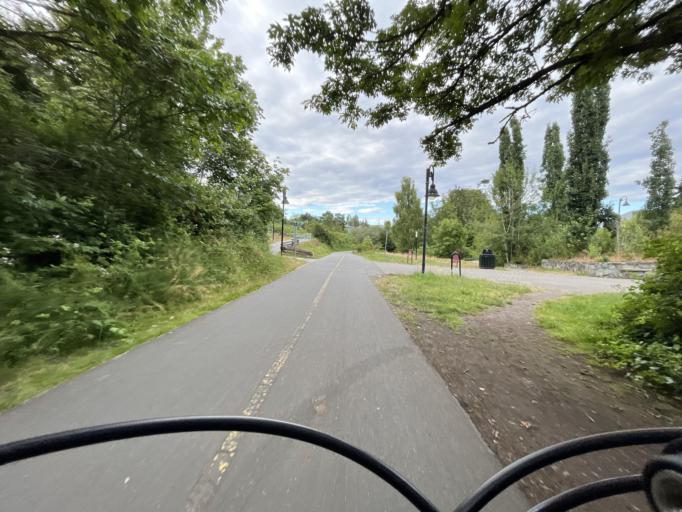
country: CA
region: British Columbia
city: Victoria
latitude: 48.4446
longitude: -123.3791
